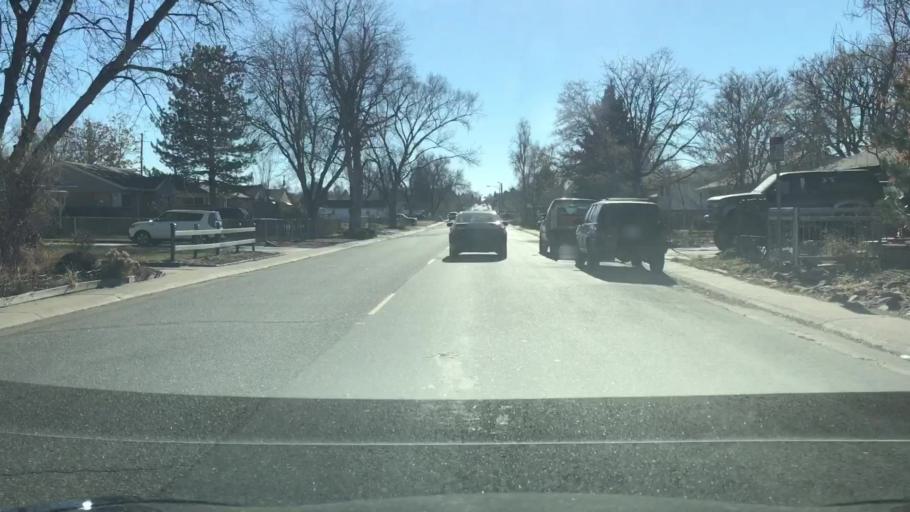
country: US
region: Colorado
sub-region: Adams County
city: Aurora
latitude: 39.7432
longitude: -104.8847
